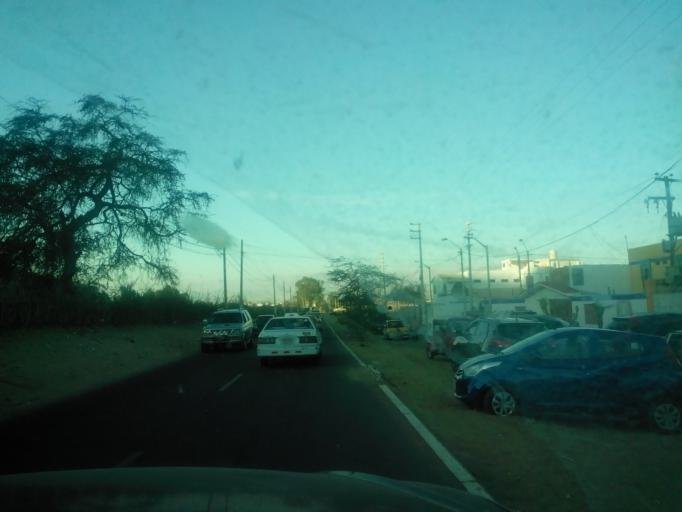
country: PE
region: Ica
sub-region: Provincia de Ica
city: Ica
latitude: -14.0858
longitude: -75.7561
